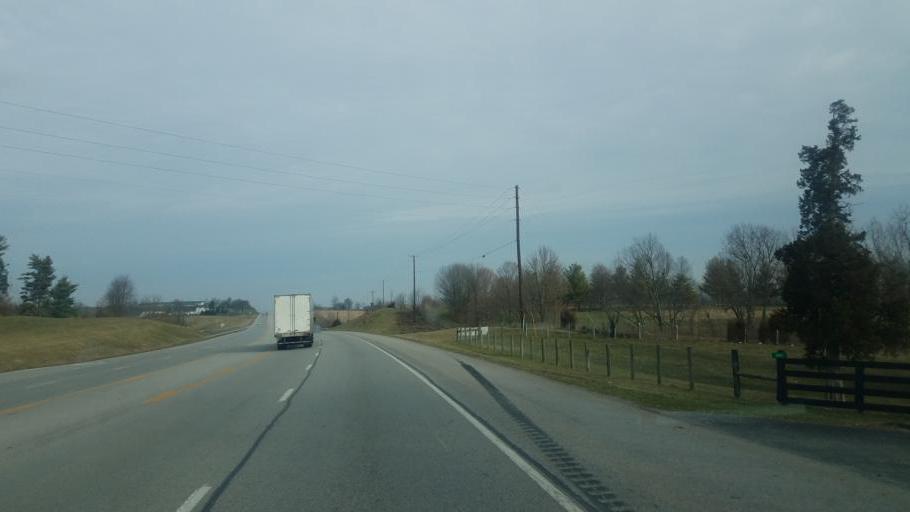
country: US
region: Kentucky
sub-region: Boyle County
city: Junction City
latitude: 37.6012
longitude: -84.7736
